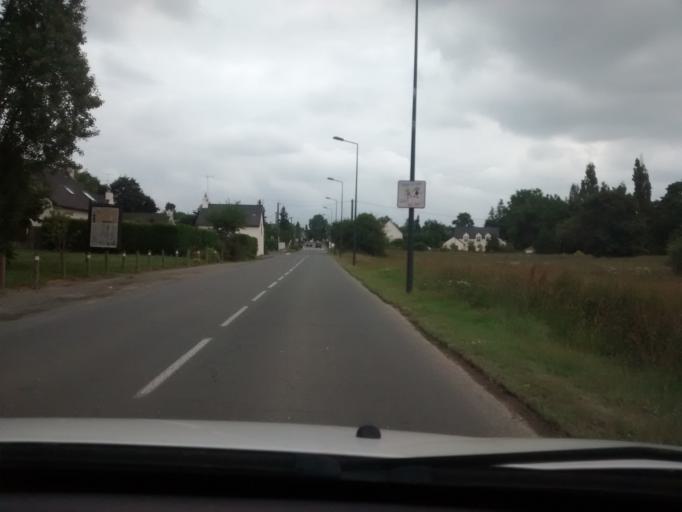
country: FR
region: Brittany
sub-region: Departement d'Ille-et-Vilaine
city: Liffre
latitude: 48.2065
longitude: -1.5095
